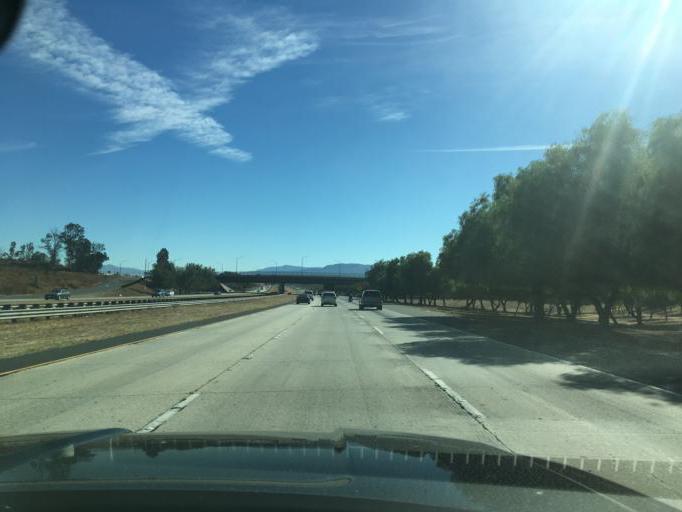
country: US
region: California
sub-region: Riverside County
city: Murrieta
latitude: 33.5563
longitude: -117.1950
